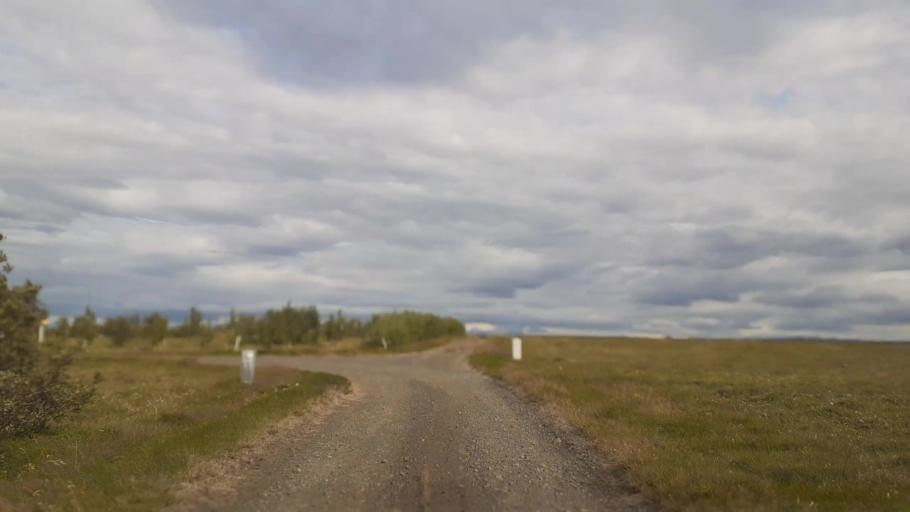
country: IS
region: South
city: Vestmannaeyjar
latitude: 63.7729
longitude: -20.2986
